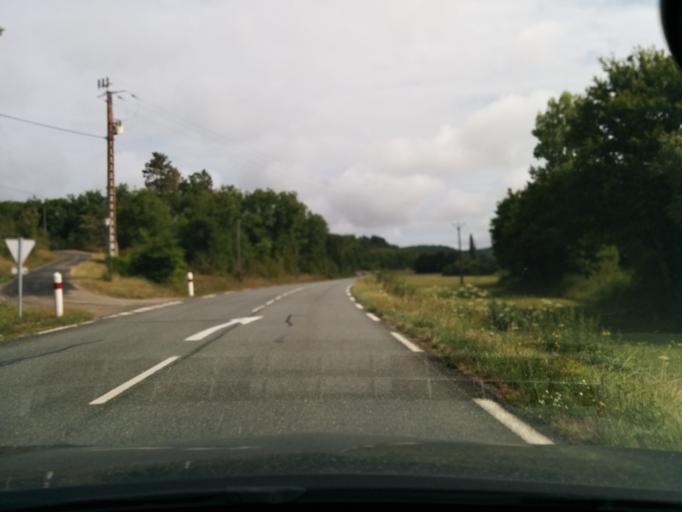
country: FR
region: Midi-Pyrenees
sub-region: Departement du Lot
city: Le Vigan
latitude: 44.7015
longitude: 1.4795
